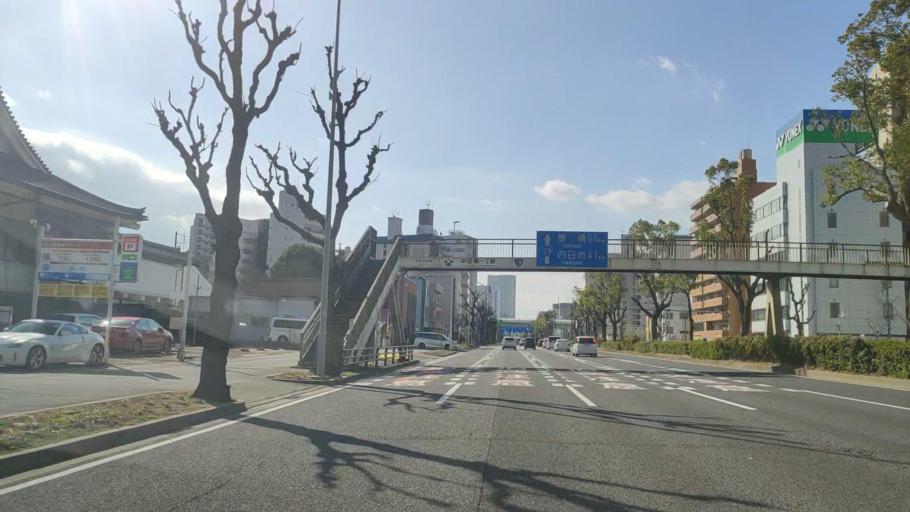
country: JP
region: Aichi
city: Nagoya-shi
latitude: 35.1554
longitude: 136.8988
